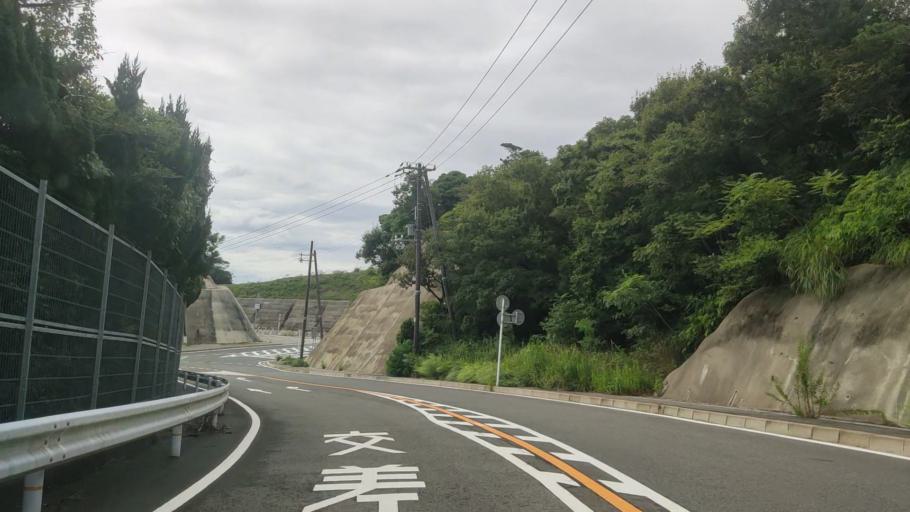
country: JP
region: Wakayama
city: Tanabe
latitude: 33.6665
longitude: 135.3669
